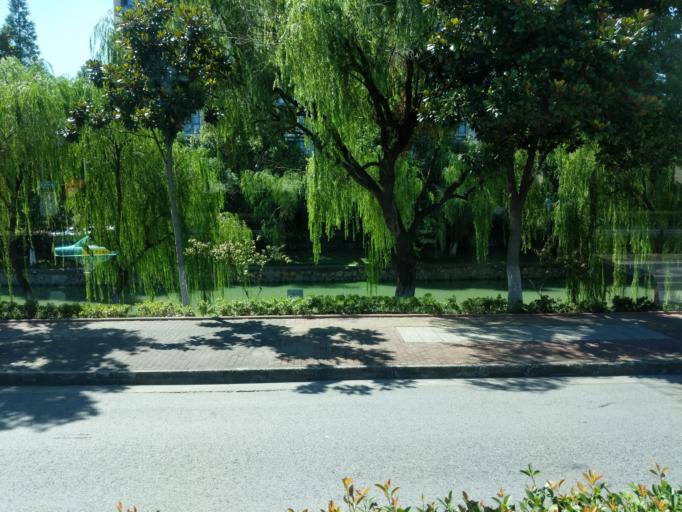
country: CN
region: Jiangsu Sheng
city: Pingjianglu
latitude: 31.3217
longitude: 120.6557
